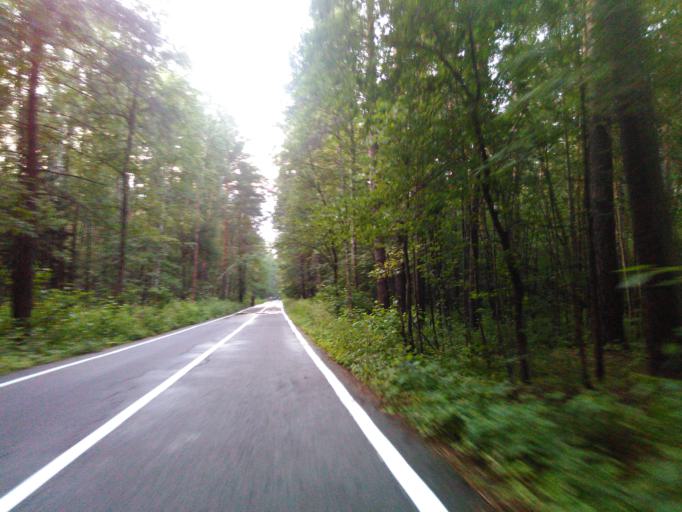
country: RU
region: Moscow
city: Babushkin
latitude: 55.8547
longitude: 37.7252
